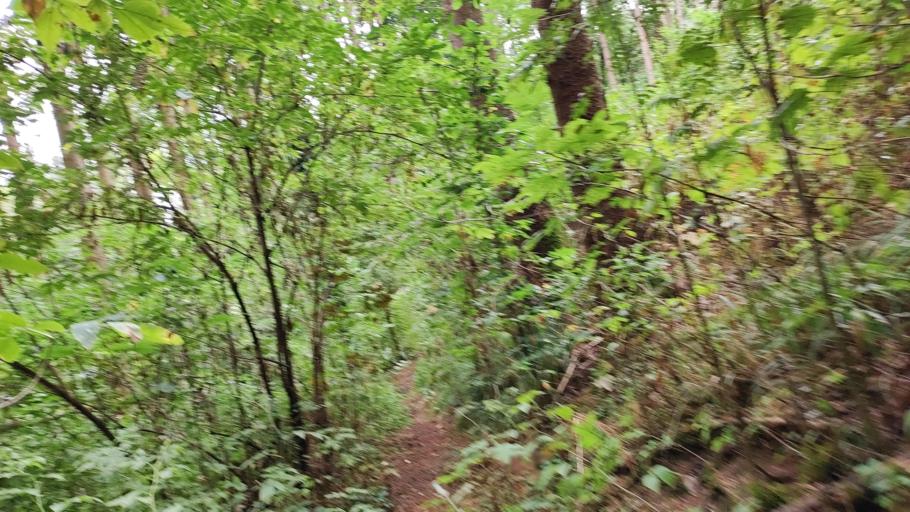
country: DE
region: Bavaria
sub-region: Swabia
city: Jettingen-Scheppach
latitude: 48.3746
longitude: 10.4048
